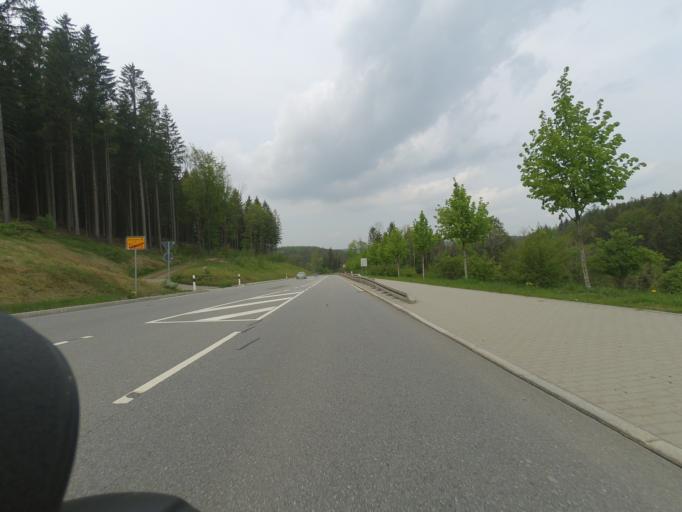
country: DE
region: Saxony
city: Zoblitz
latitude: 50.6595
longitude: 13.2196
